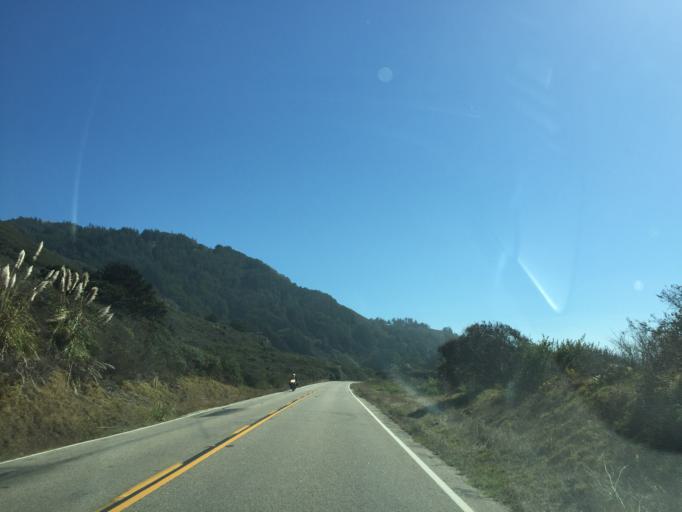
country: US
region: California
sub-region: Monterey County
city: King City
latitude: 35.9266
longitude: -121.4668
